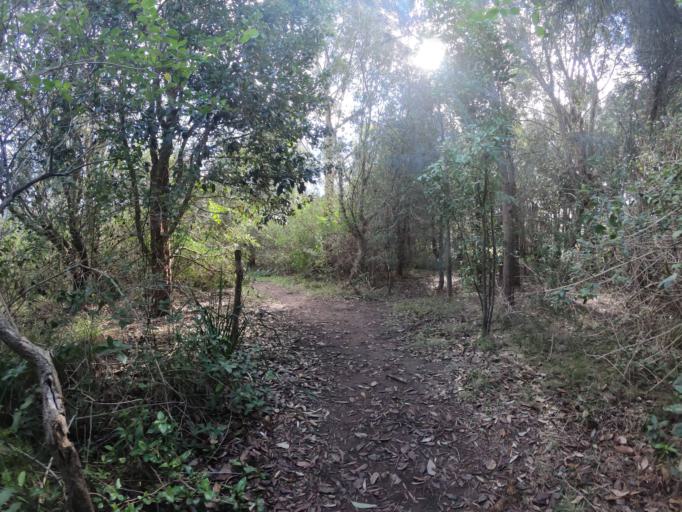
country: AU
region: New South Wales
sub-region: Wollongong
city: Bulli
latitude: -34.3242
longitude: 150.9227
